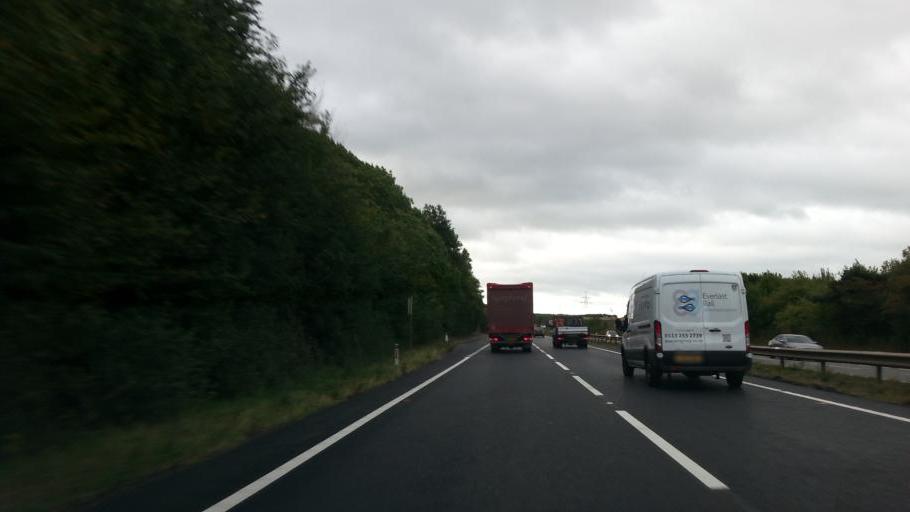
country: GB
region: England
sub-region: Lincolnshire
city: Great Gonerby
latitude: 52.9345
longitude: -0.6847
